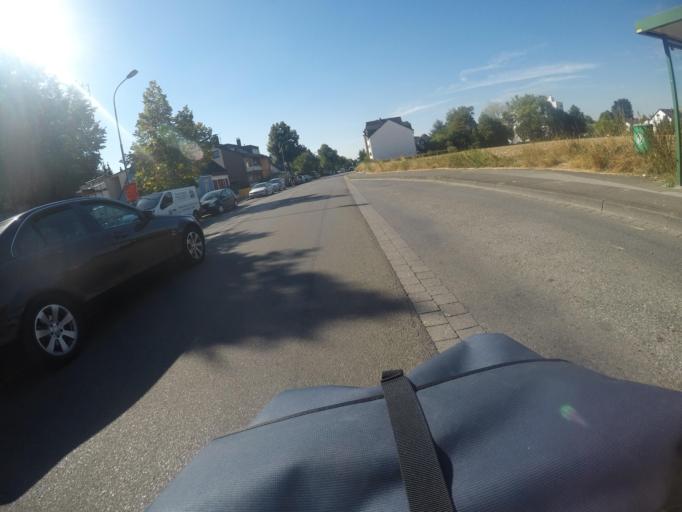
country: DE
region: North Rhine-Westphalia
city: Leichlingen
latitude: 51.0815
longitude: 6.9959
